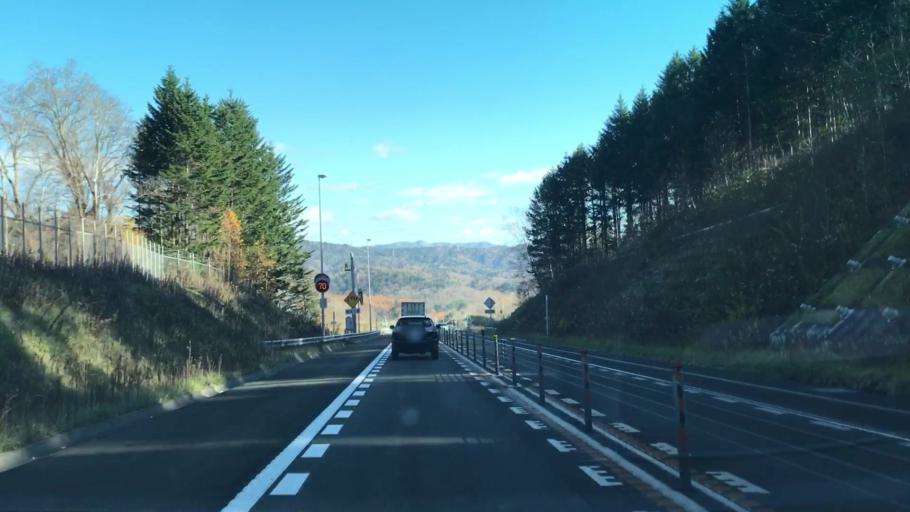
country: JP
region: Hokkaido
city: Shimo-furano
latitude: 42.9199
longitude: 142.1722
